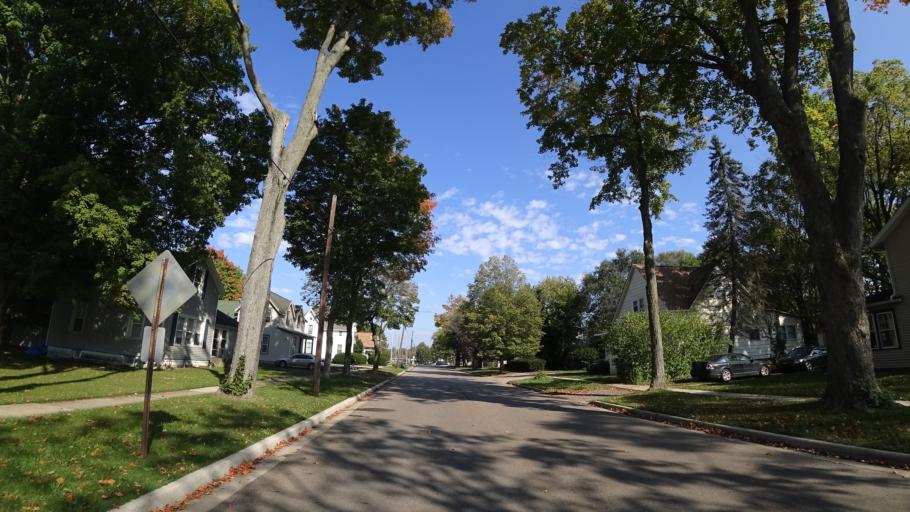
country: US
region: Michigan
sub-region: Saint Joseph County
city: Three Rivers
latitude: 41.9415
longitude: -85.6370
